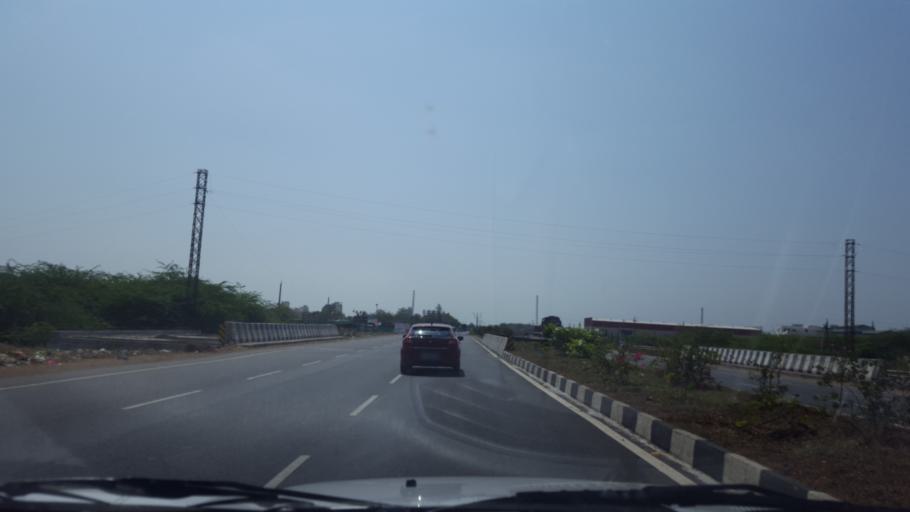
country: IN
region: Andhra Pradesh
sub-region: Prakasam
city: Addanki
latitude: 15.6920
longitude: 80.0185
